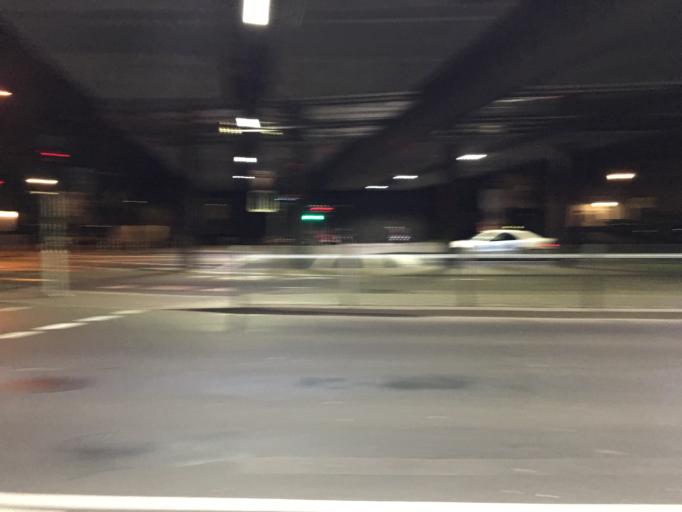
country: DE
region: North Rhine-Westphalia
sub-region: Regierungsbezirk Dusseldorf
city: Dusseldorf
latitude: 51.2091
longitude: 6.7828
